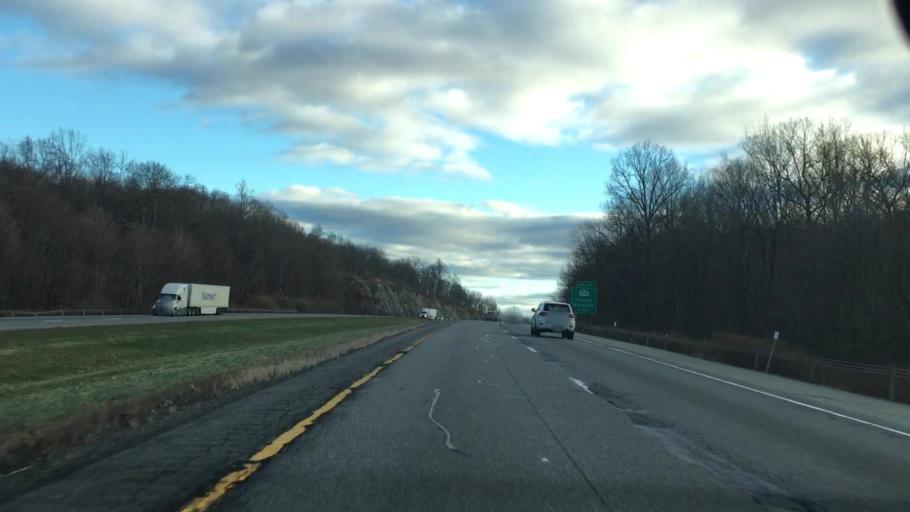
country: US
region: New York
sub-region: Putnam County
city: Brewster Hill
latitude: 41.4432
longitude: -73.6337
